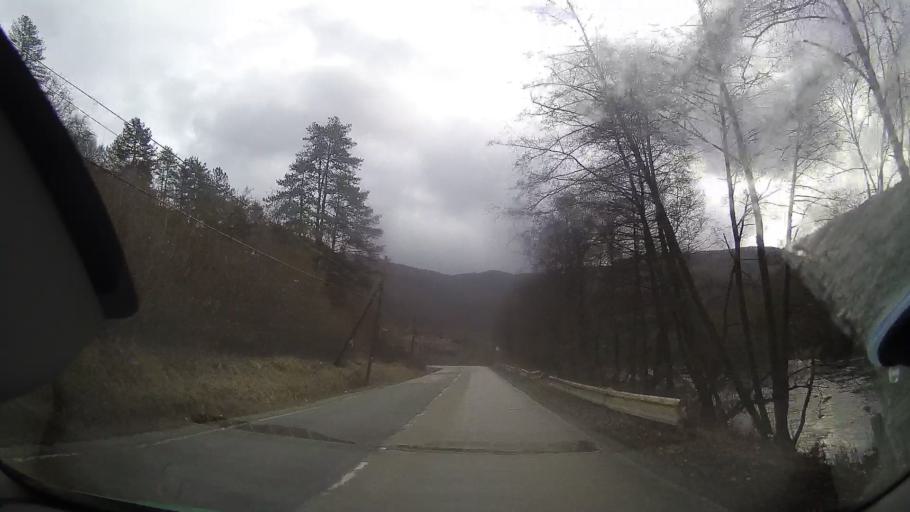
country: RO
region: Cluj
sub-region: Comuna Moldovenesti
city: Moldovenesti
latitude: 46.5062
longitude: 23.6065
